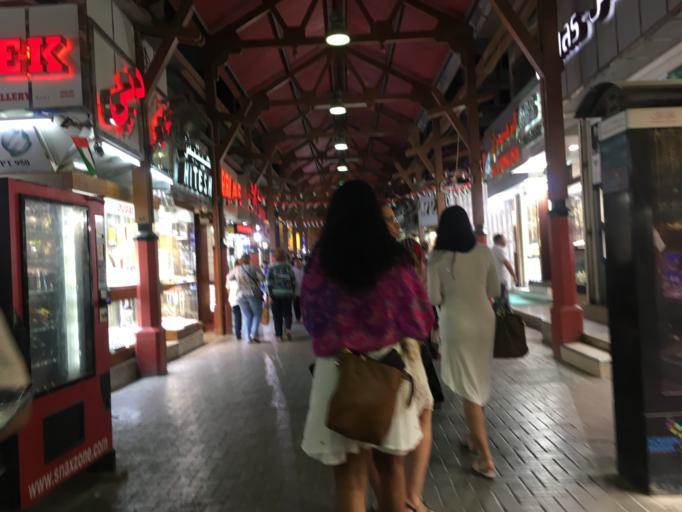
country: AE
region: Ash Shariqah
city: Sharjah
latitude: 25.2693
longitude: 55.2974
